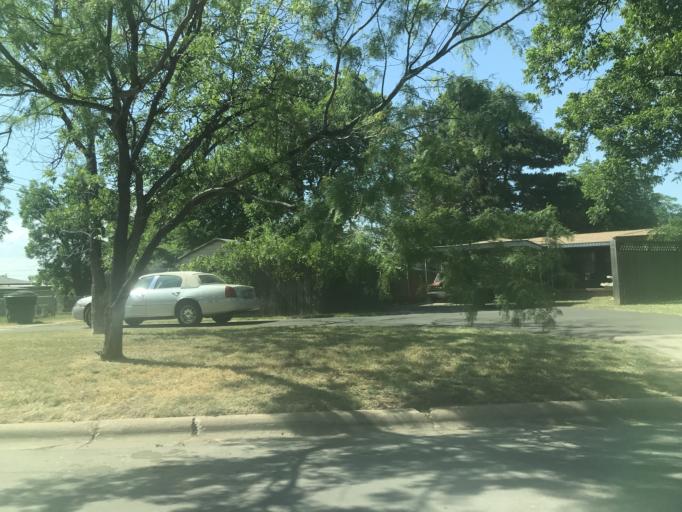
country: US
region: Texas
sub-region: Taylor County
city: Abilene
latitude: 32.4341
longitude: -99.7518
